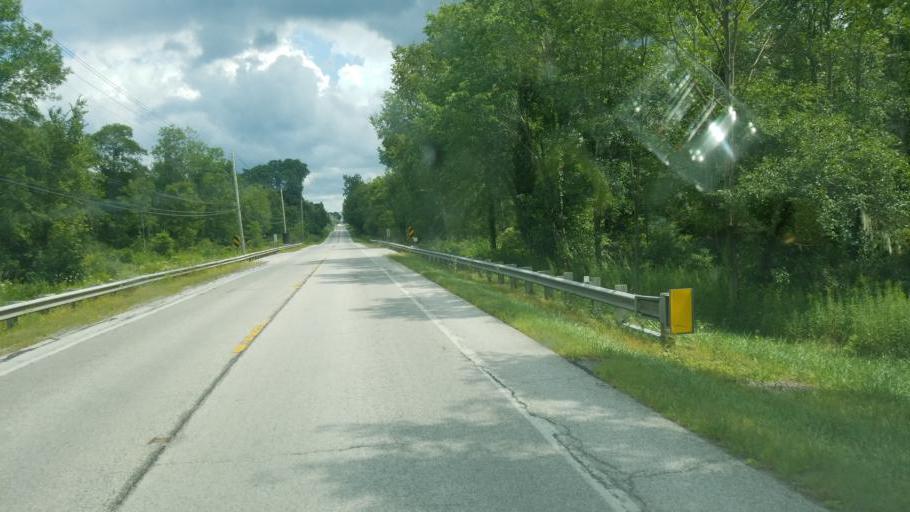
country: US
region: Ohio
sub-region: Ashtabula County
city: Andover
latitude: 41.6070
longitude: -80.6307
